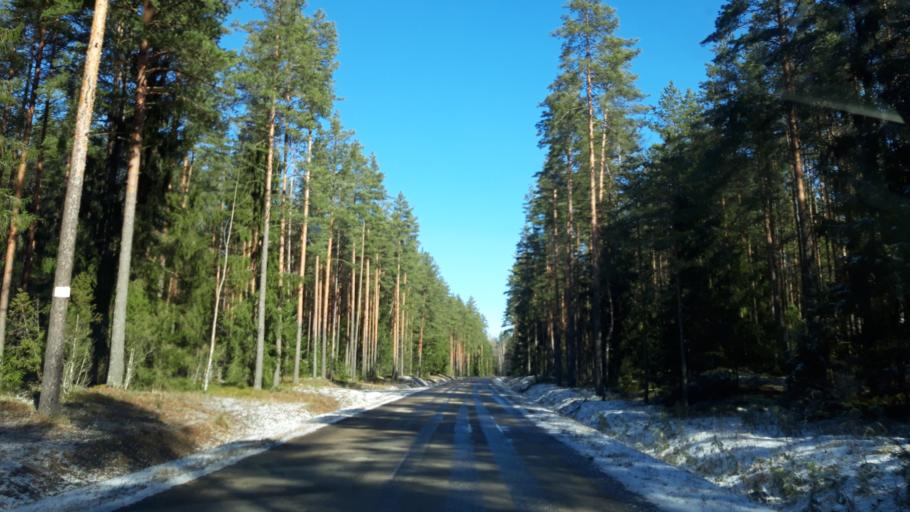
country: LV
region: Strenci
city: Strenci
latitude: 57.5817
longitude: 25.7142
